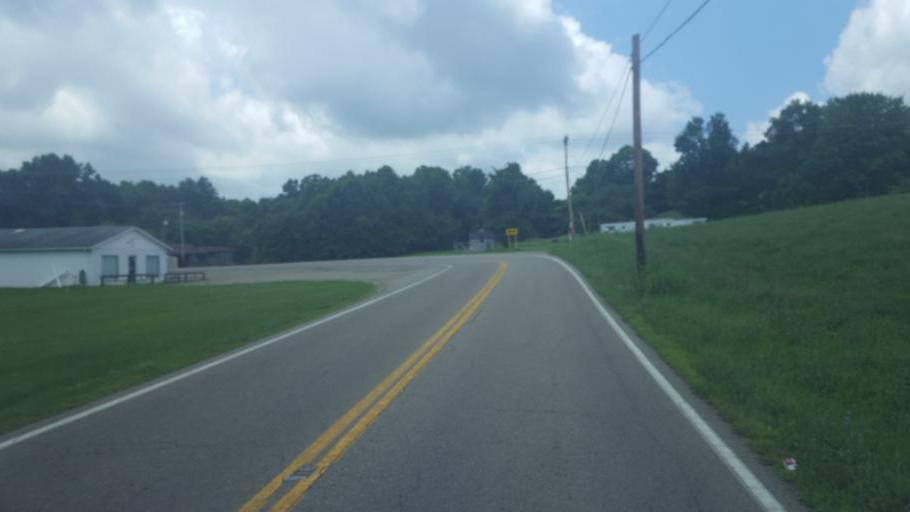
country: US
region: Ohio
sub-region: Ross County
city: Kingston
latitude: 39.4608
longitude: -82.7499
